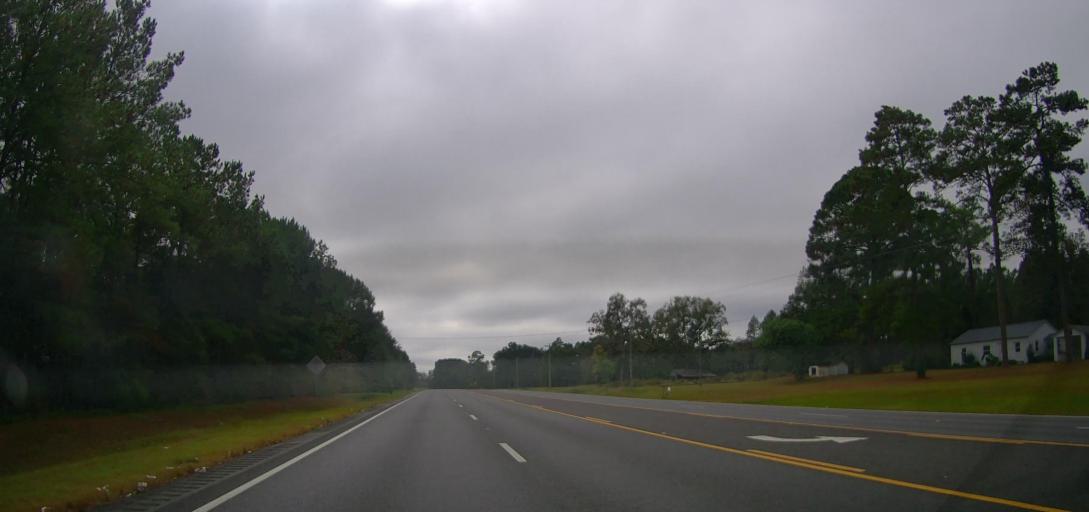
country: US
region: Georgia
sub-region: Thomas County
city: Thomasville
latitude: 30.9725
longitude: -83.8893
